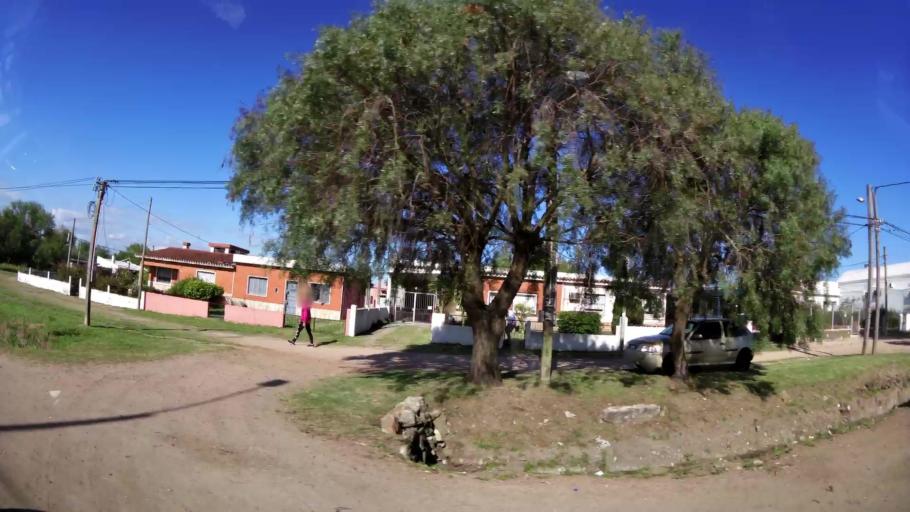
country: UY
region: Canelones
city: La Paz
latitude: -34.8154
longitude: -56.1580
